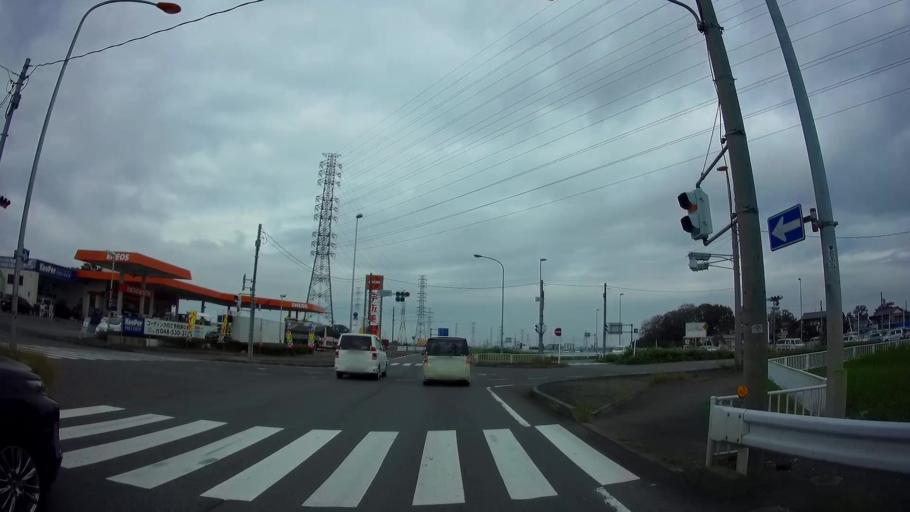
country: JP
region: Saitama
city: Menuma
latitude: 36.1801
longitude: 139.3565
